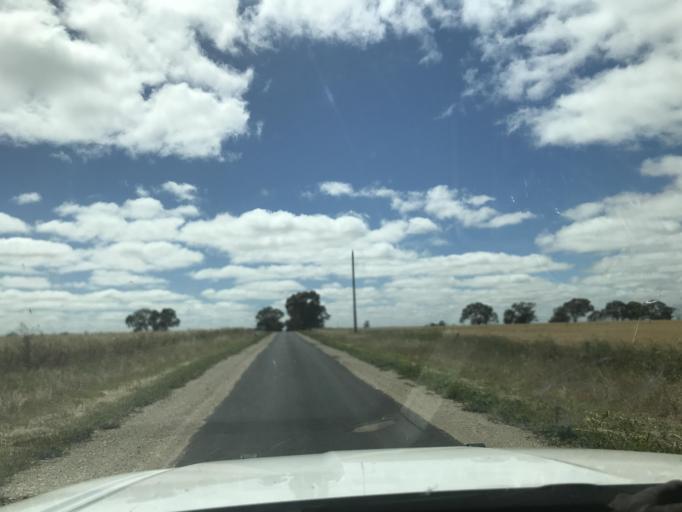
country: AU
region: South Australia
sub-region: Tatiara
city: Bordertown
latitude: -36.2791
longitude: 141.1211
